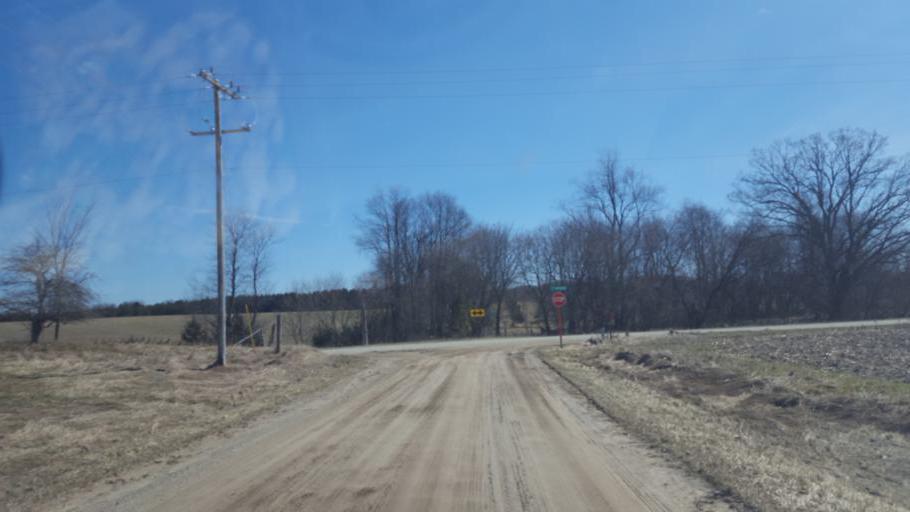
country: US
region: Michigan
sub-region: Montcalm County
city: Edmore
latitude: 43.4733
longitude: -85.0456
